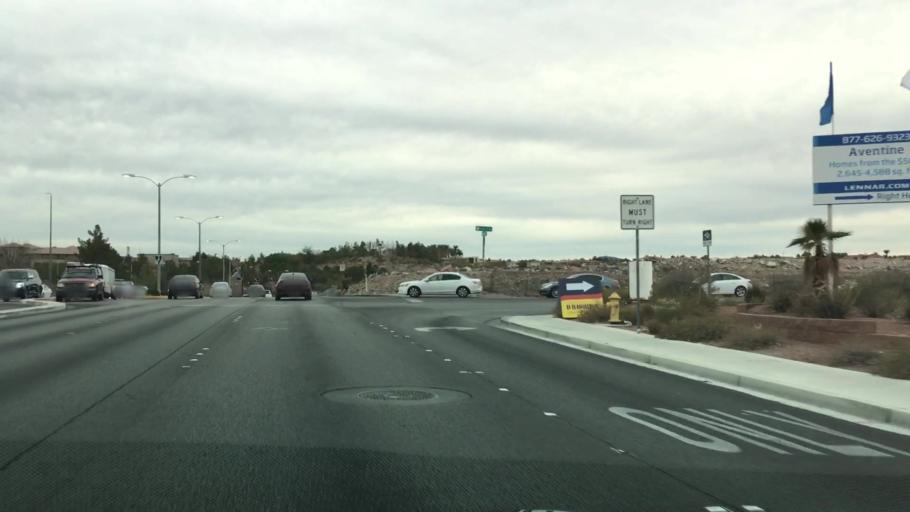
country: US
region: Nevada
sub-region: Clark County
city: Whitney
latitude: 35.9870
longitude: -115.0914
